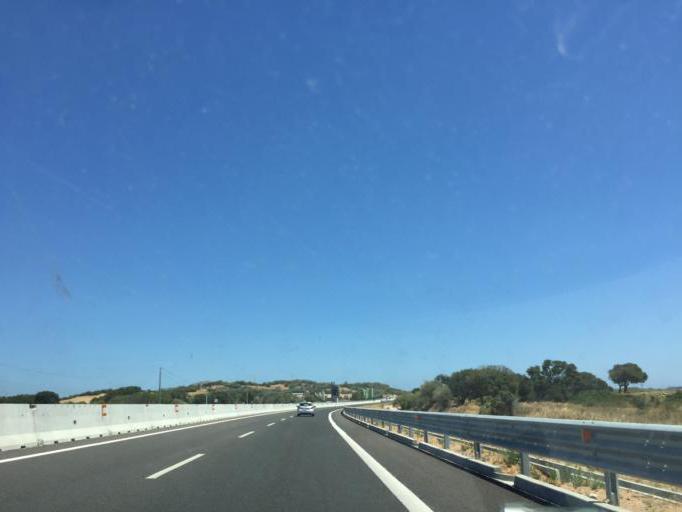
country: IT
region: Sardinia
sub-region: Provincia di Olbia-Tempio
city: Loiri Porto San Paolo
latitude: 40.8791
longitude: 9.4656
